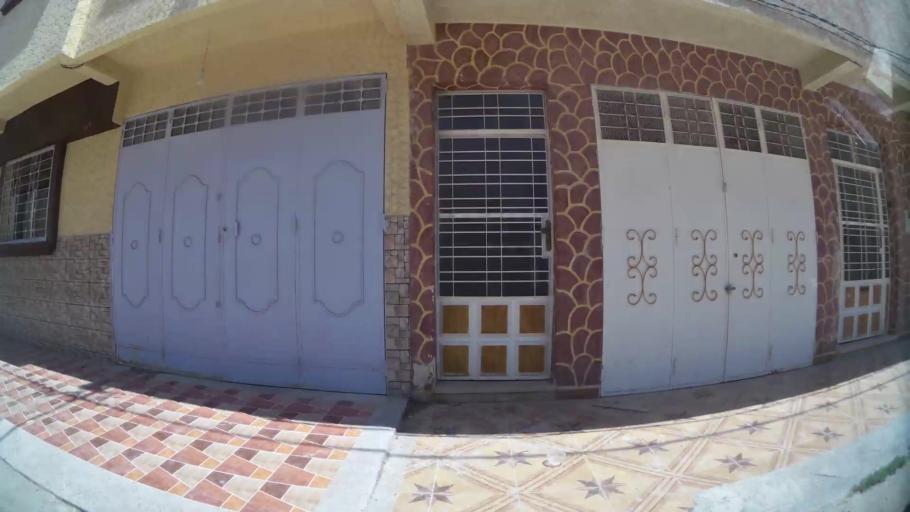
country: MA
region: Oriental
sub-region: Oujda-Angad
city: Oujda
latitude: 34.6950
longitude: -1.8848
